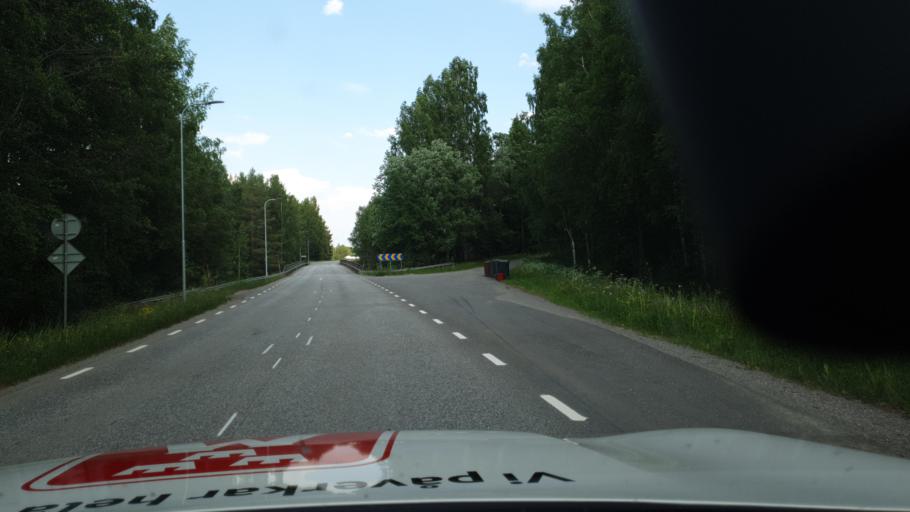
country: SE
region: Vaesterbotten
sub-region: Skelleftea Kommun
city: Viken
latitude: 64.7388
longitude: 20.7668
